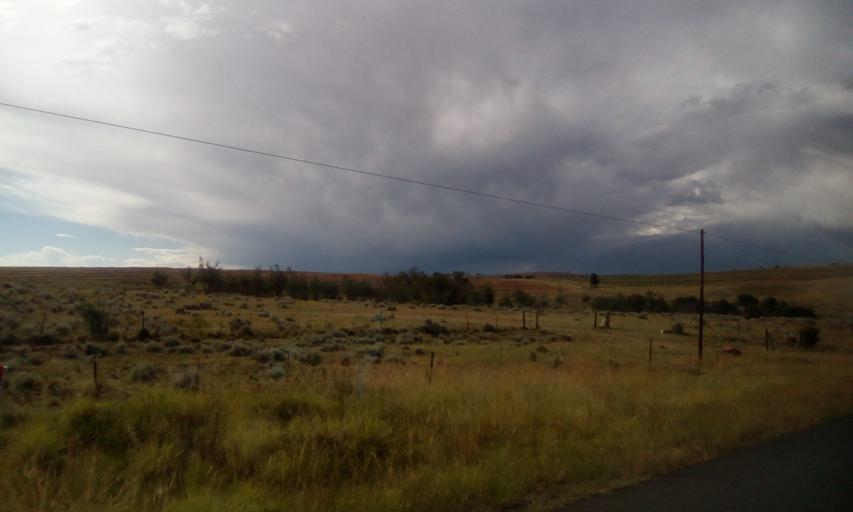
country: ZA
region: Orange Free State
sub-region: Thabo Mofutsanyana District Municipality
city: Ladybrand
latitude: -29.2169
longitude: 27.4532
